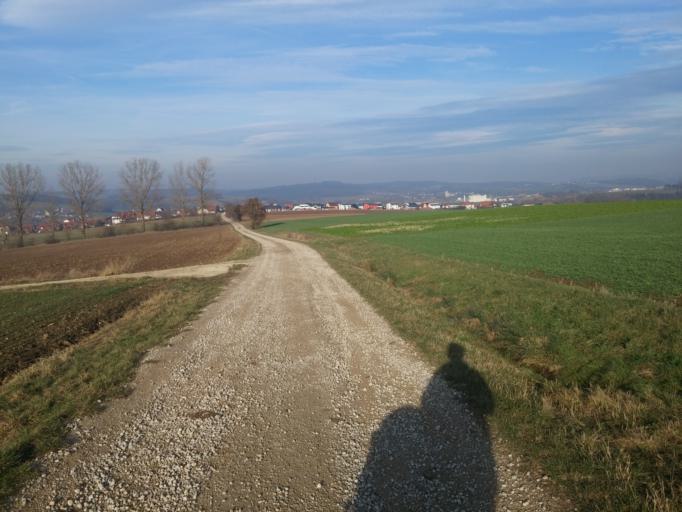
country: DE
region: Bavaria
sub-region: Upper Franconia
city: Grossheirath
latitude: 50.1667
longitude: 10.9557
